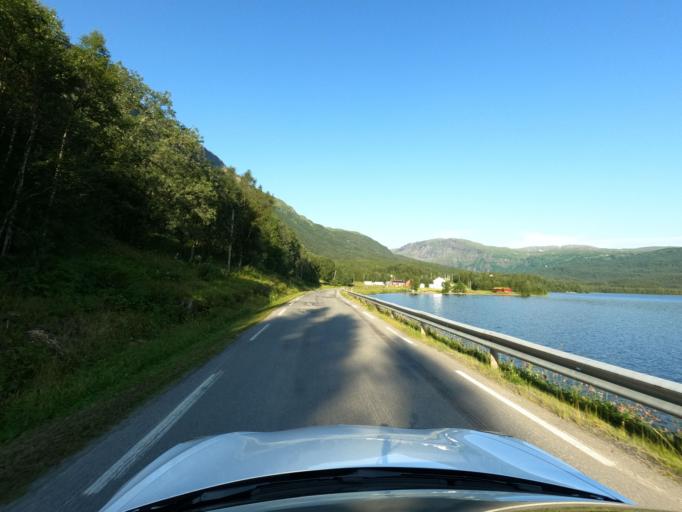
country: NO
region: Troms
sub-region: Gratangen
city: Gratangen
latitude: 68.5615
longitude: 17.6844
